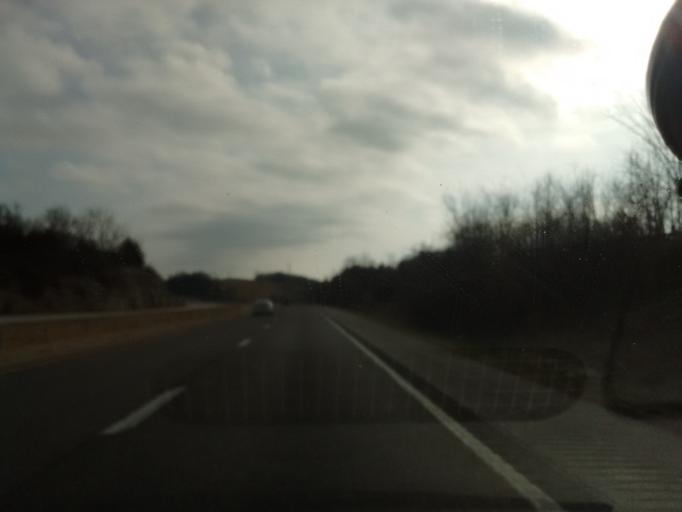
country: US
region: Missouri
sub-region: Cooper County
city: Boonville
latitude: 38.9358
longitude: -92.9797
